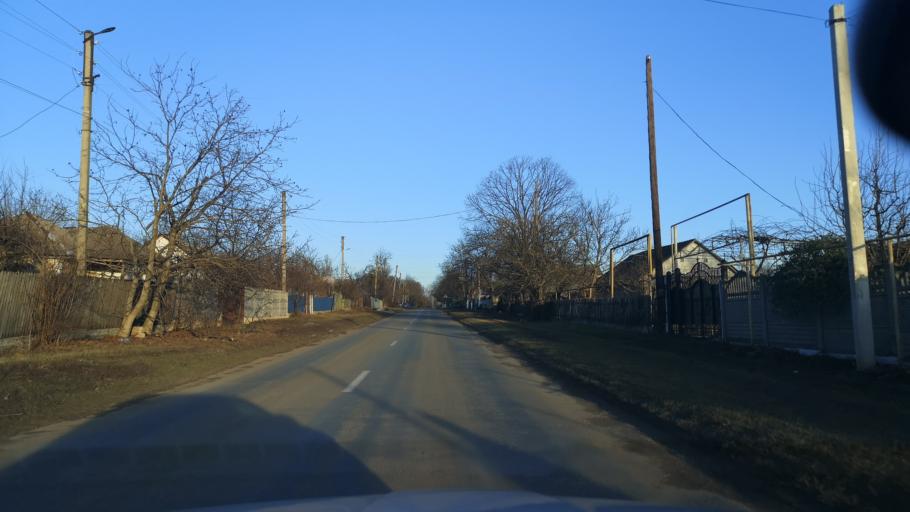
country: MD
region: Orhei
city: Orhei
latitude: 47.2865
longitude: 28.8524
